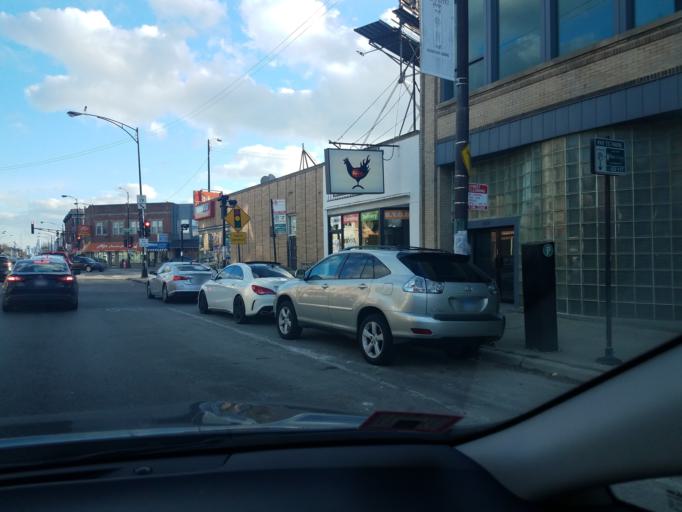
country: US
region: Illinois
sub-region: Cook County
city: Lincolnwood
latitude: 41.9542
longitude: -87.7200
